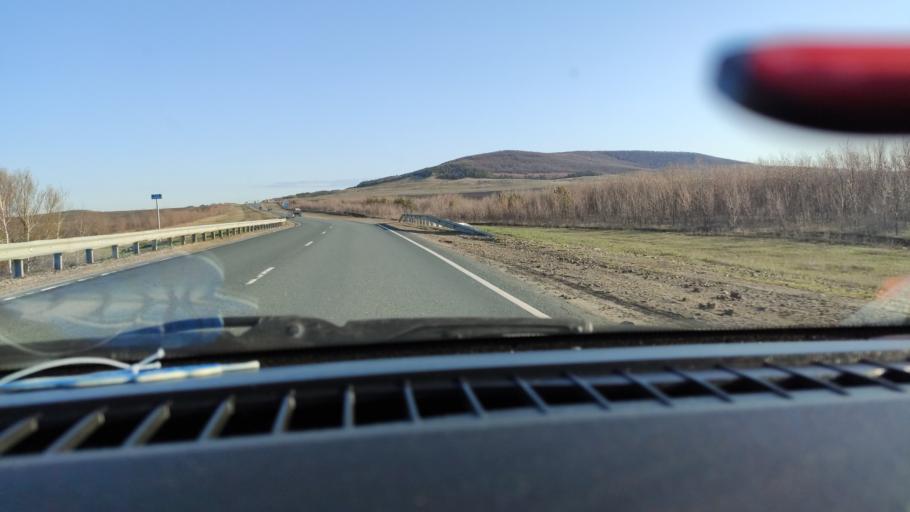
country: RU
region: Saratov
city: Alekseyevka
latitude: 52.2821
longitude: 47.9325
